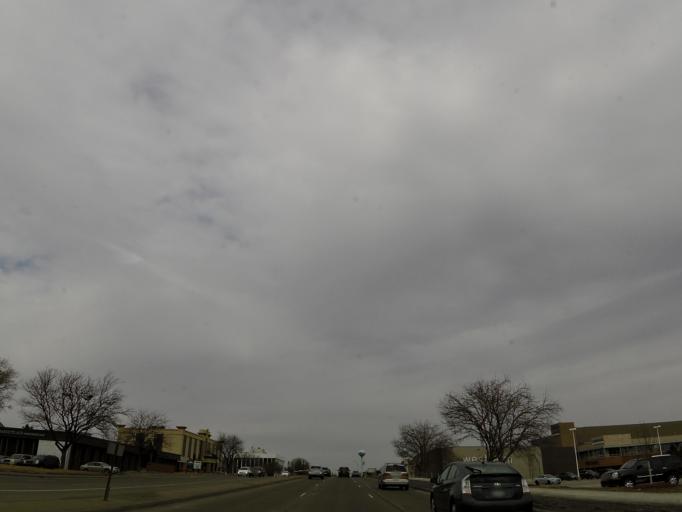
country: US
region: Minnesota
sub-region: Hennepin County
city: Edina
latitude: 44.8686
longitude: -93.3288
